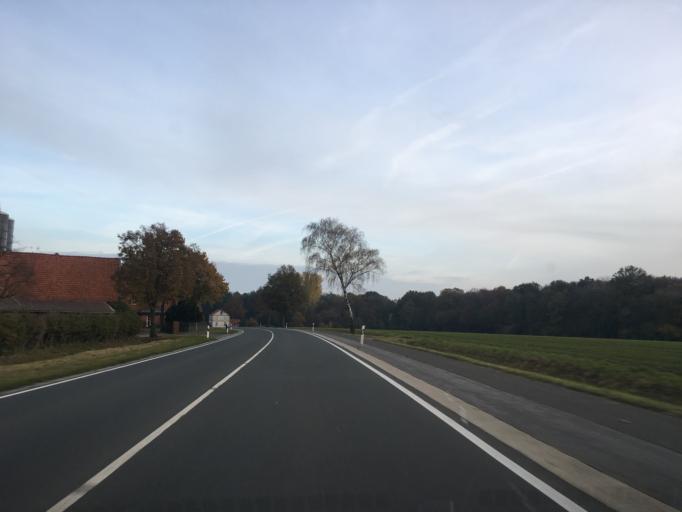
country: DE
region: North Rhine-Westphalia
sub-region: Regierungsbezirk Munster
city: Steinfurt
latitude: 52.1349
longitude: 7.3732
